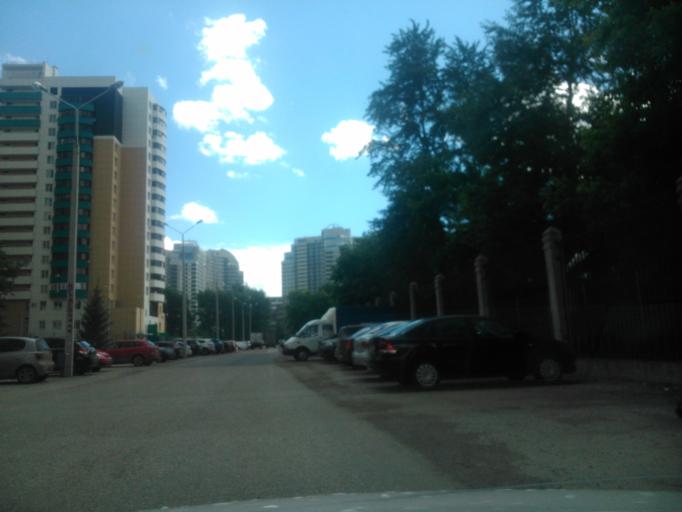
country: RU
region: Perm
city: Perm
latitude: 58.0002
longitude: 56.2671
